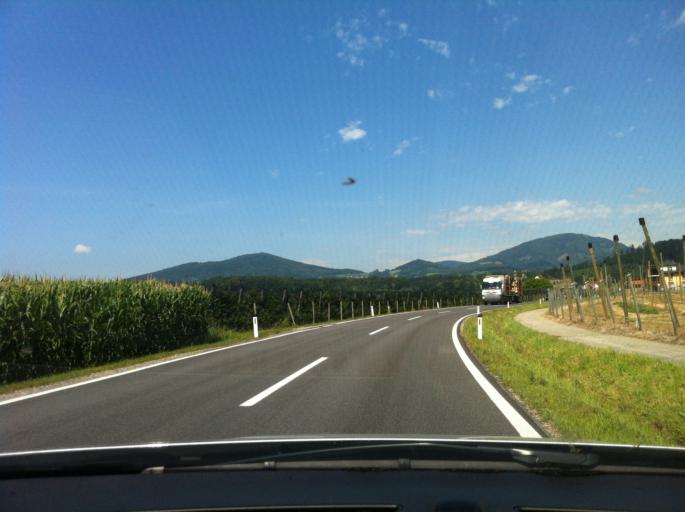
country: AT
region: Styria
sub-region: Politischer Bezirk Weiz
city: Floing
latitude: 47.2433
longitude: 15.7369
